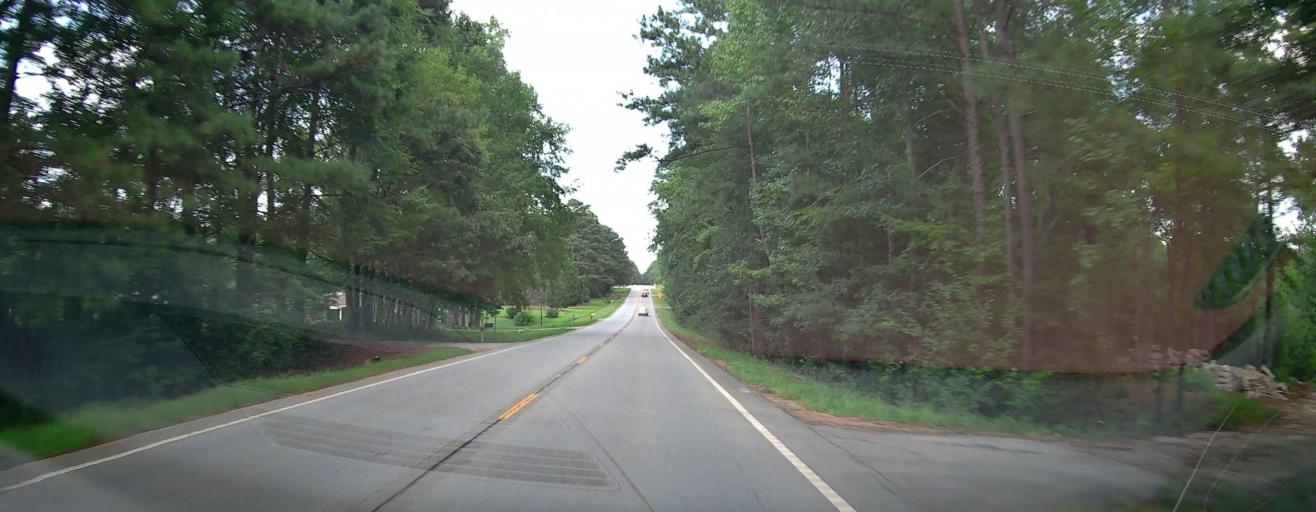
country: US
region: Georgia
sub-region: Coweta County
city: Senoia
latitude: 33.2492
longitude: -84.5624
